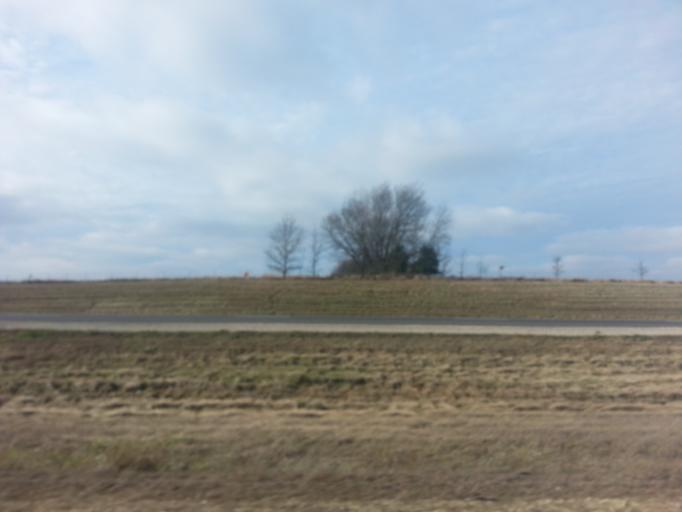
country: US
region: Illinois
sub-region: Ogle County
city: Davis Junction
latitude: 42.1441
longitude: -89.0232
